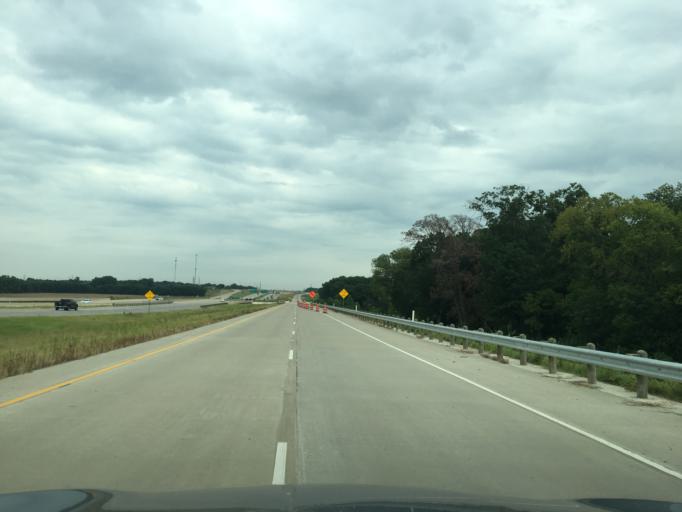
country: US
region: Texas
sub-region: Collin County
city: Melissa
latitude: 33.2980
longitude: -96.5911
